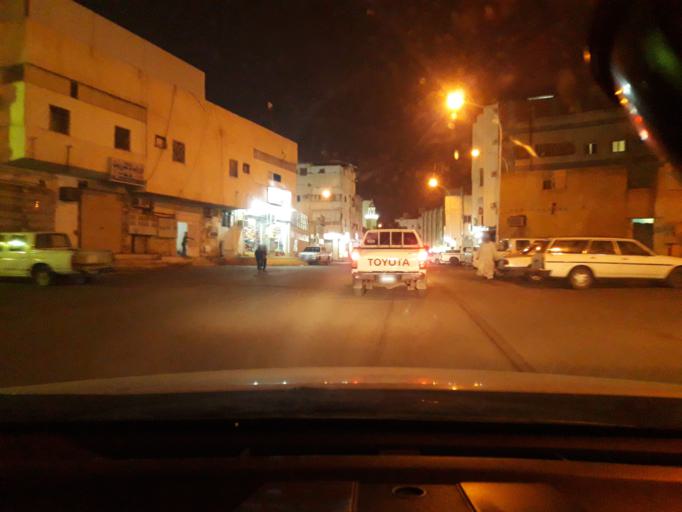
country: SA
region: Al Madinah al Munawwarah
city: Medina
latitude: 24.4659
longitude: 39.6285
